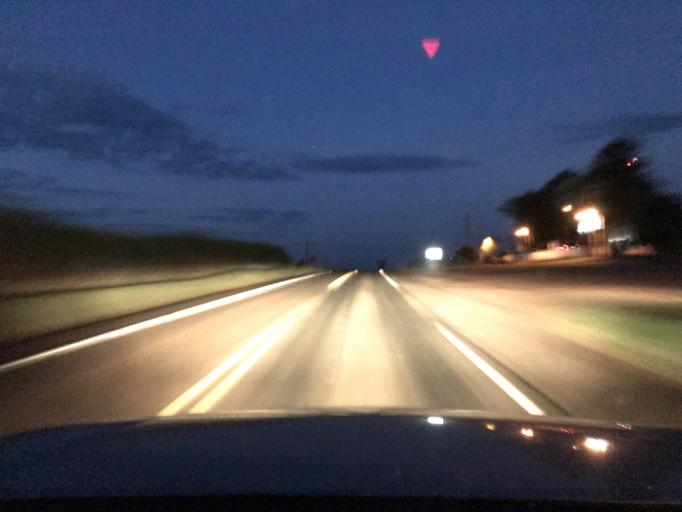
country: PY
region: Canindeyu
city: Salto del Guaira
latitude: -24.1019
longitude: -54.2293
